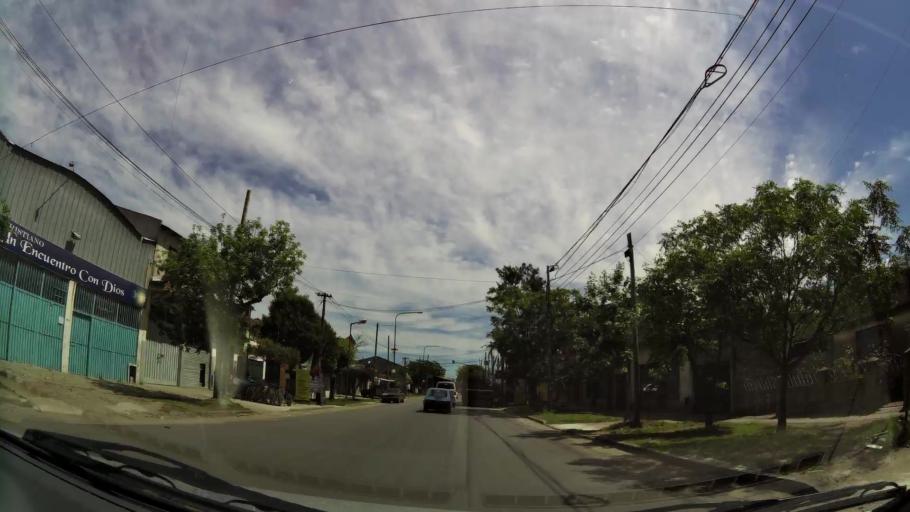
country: AR
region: Buenos Aires
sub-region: Partido de Quilmes
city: Quilmes
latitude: -34.7489
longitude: -58.2943
